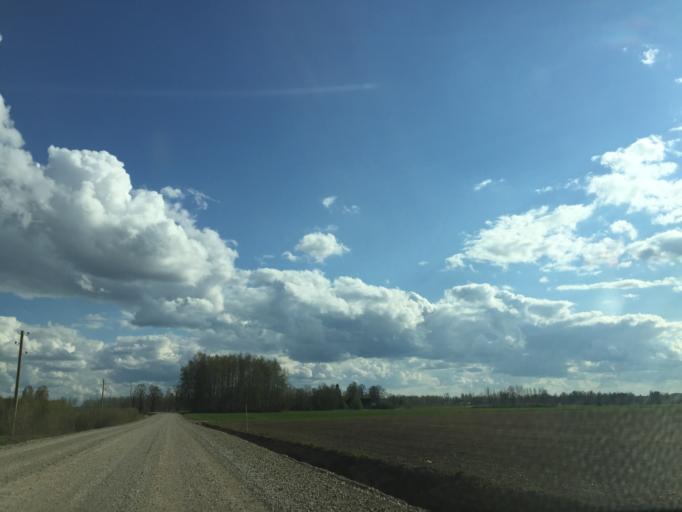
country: LV
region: Beverina
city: Murmuiza
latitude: 57.4075
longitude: 25.5105
